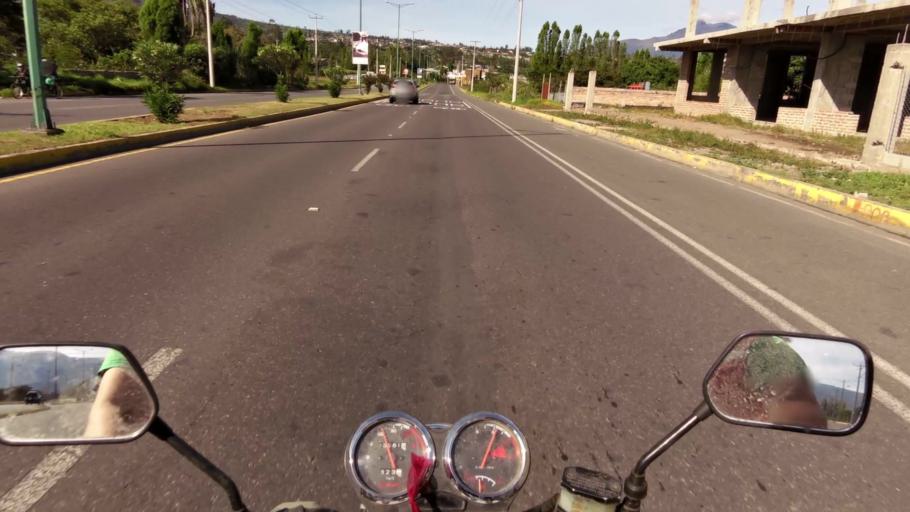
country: EC
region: Imbabura
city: Ibarra
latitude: 0.3318
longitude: -78.1489
